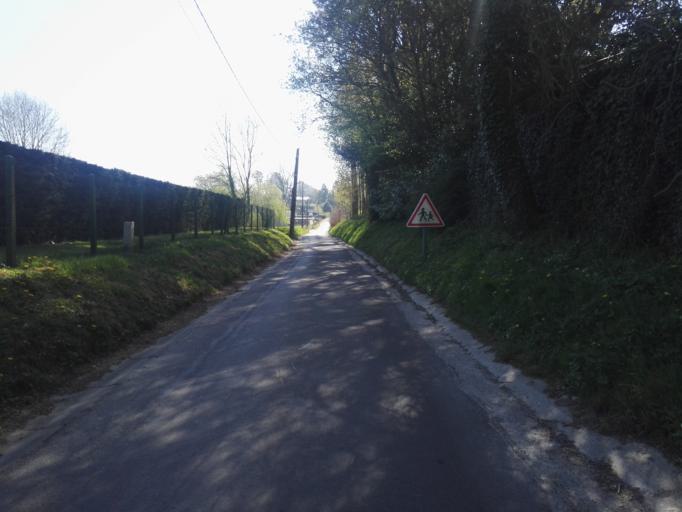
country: FR
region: Haute-Normandie
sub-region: Departement de la Seine-Maritime
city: Doudeville
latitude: 49.7503
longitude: 0.7307
